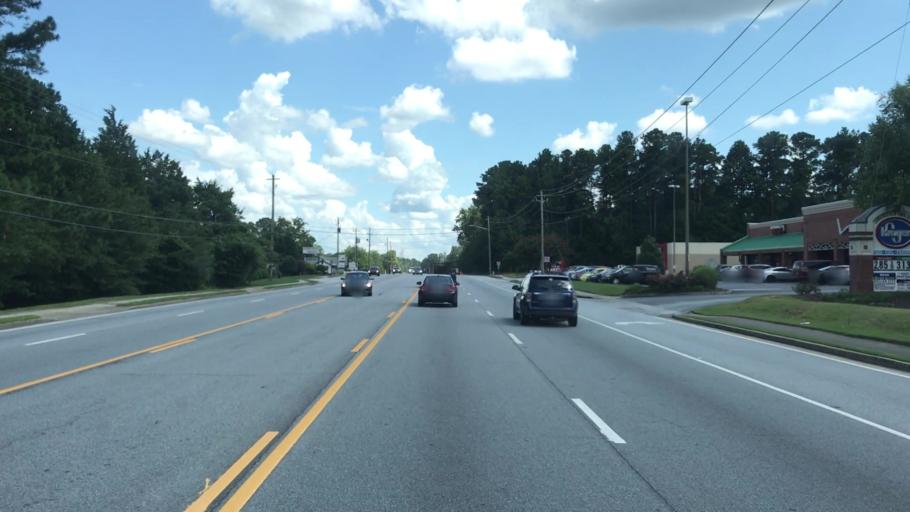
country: US
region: Georgia
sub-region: Gwinnett County
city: Lawrenceville
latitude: 33.9398
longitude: -83.9819
